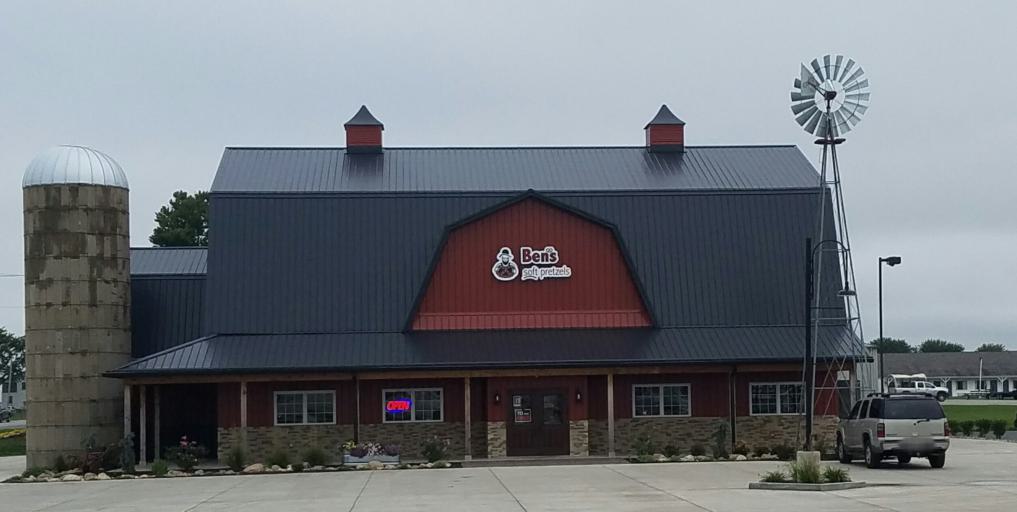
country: US
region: Indiana
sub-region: LaGrange County
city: Topeka
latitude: 41.6594
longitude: -85.5800
